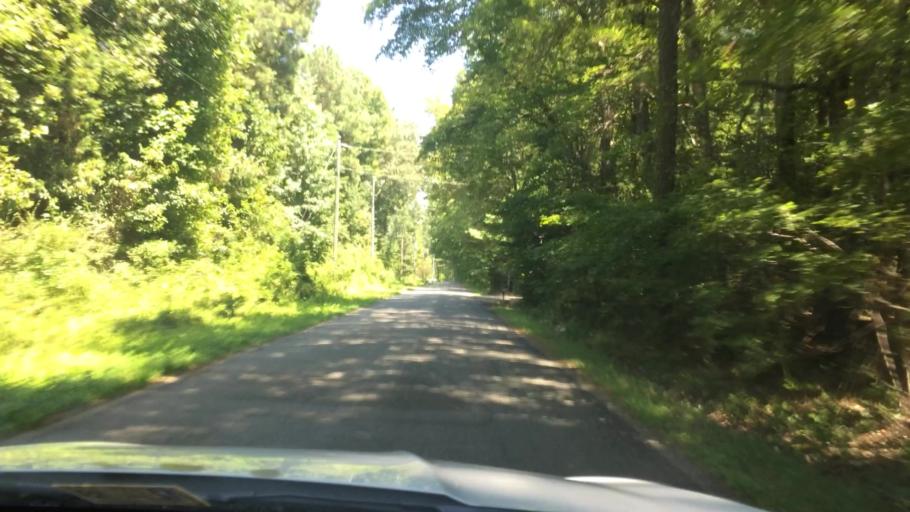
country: US
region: Virginia
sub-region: Charles City County
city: Charles City
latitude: 37.2678
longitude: -76.9444
